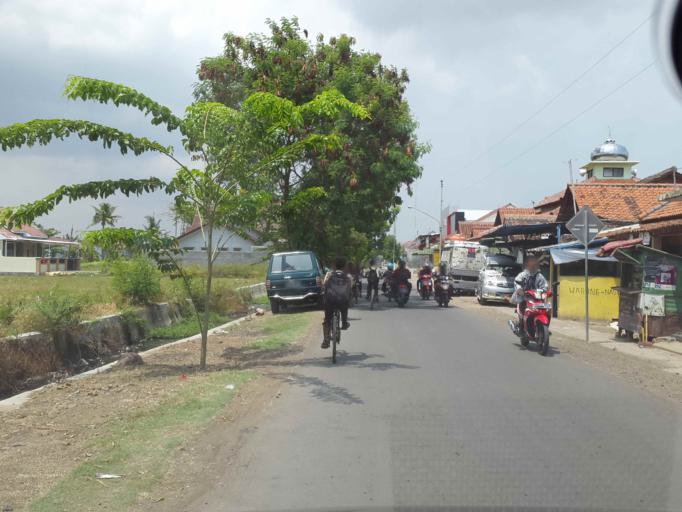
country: ID
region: Central Java
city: Dukuhturi
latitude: -6.8645
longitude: 109.0478
